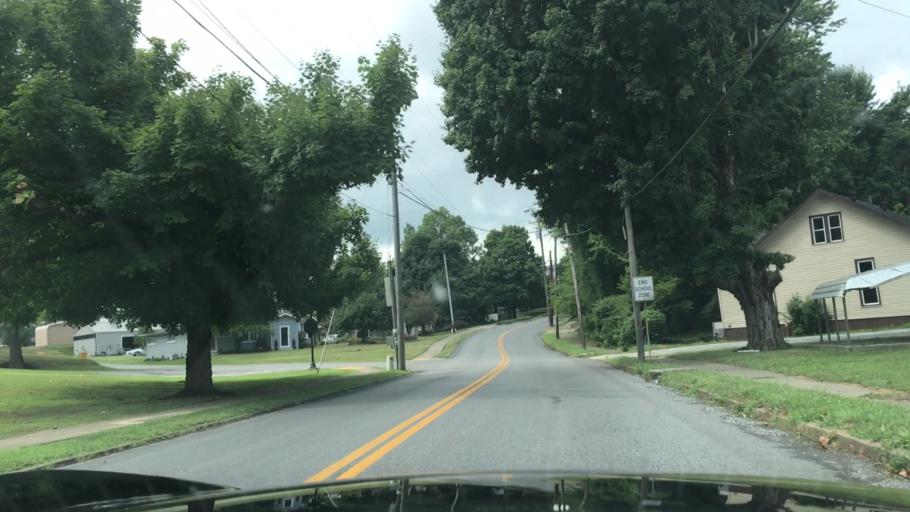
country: US
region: Kentucky
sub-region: Muhlenberg County
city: Greenville
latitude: 37.2020
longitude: -87.1754
